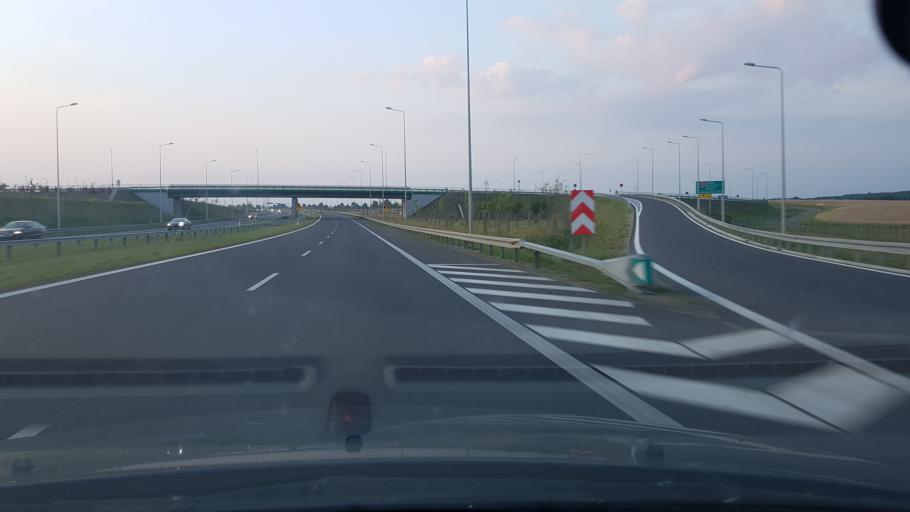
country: PL
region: Warmian-Masurian Voivodeship
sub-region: Powiat nidzicki
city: Nidzica
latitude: 53.2747
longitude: 20.4361
